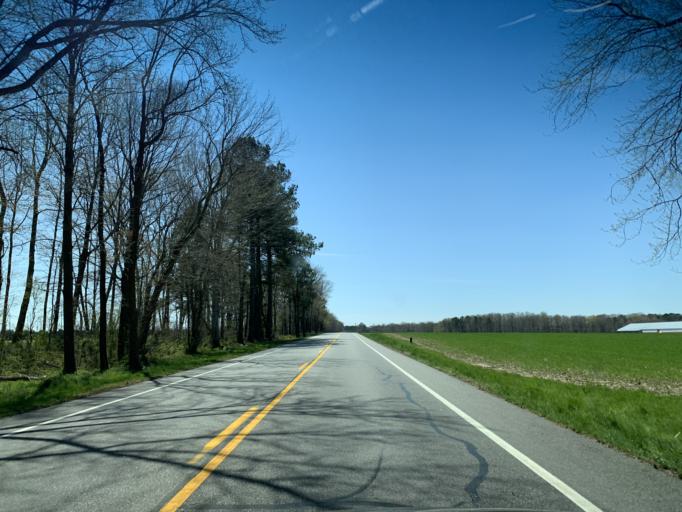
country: US
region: Maryland
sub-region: Talbot County
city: Easton
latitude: 38.8301
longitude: -76.0340
